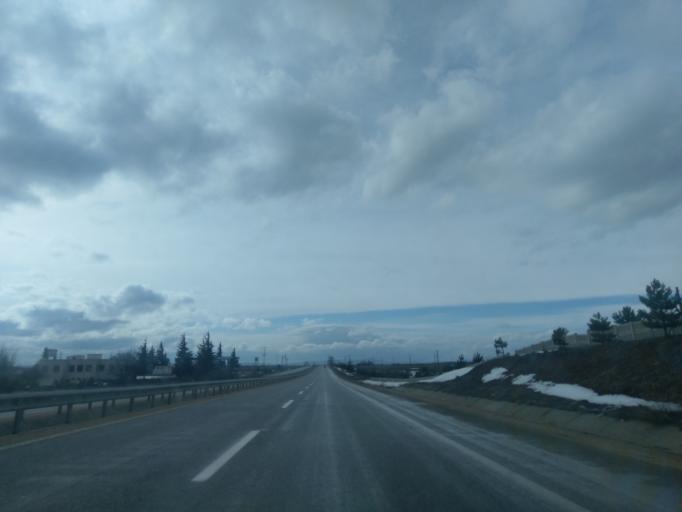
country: TR
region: Eskisehir
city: Inonu
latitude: 39.7216
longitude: 30.2387
